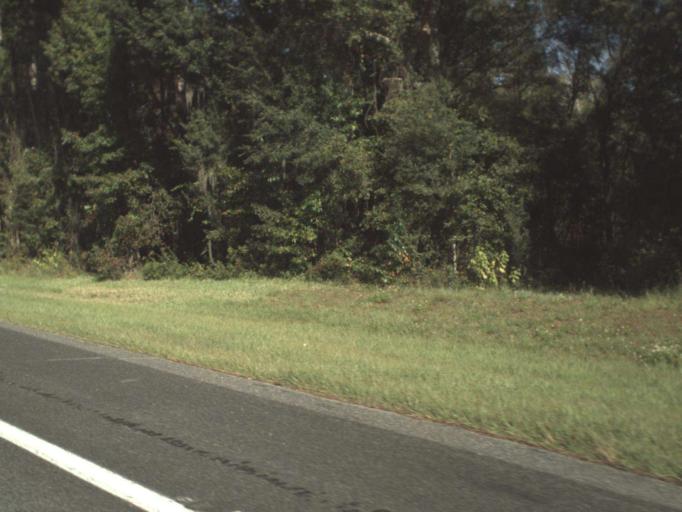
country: US
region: Florida
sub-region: Jefferson County
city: Monticello
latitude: 30.4578
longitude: -83.7702
